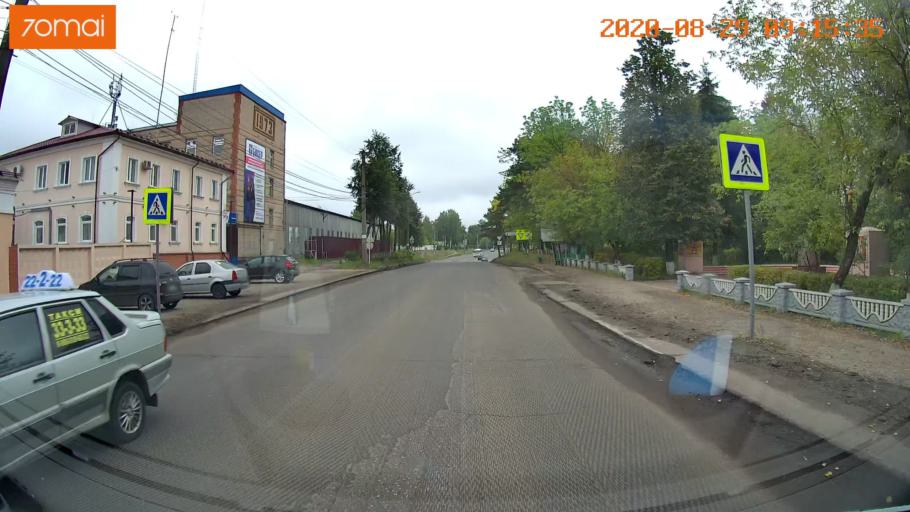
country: RU
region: Ivanovo
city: Kineshma
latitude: 57.4389
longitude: 42.1313
